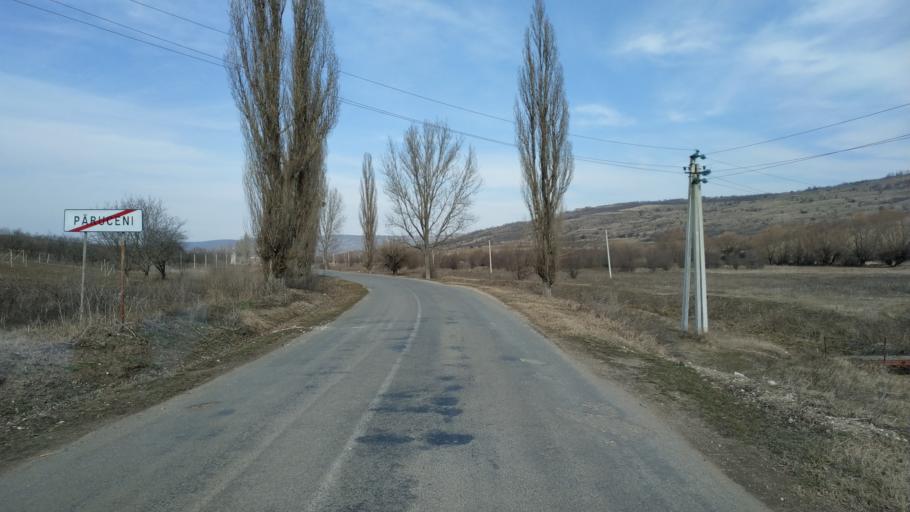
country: MD
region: Nisporeni
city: Nisporeni
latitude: 47.1542
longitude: 28.1079
